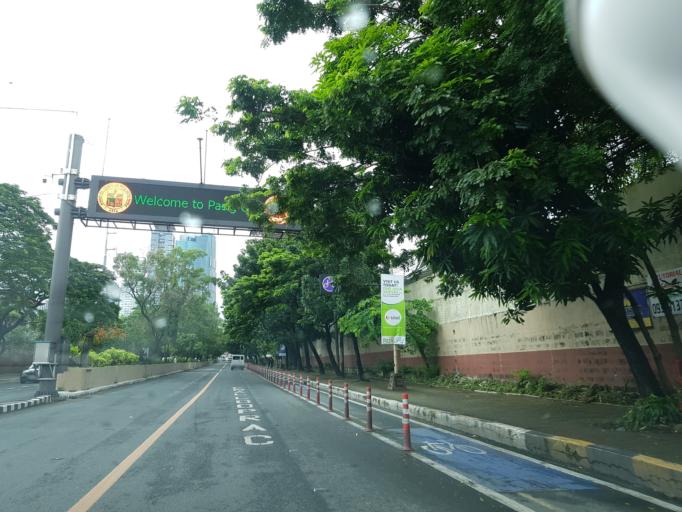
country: PH
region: Metro Manila
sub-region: Pasig
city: Pasig City
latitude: 14.5844
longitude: 121.0704
